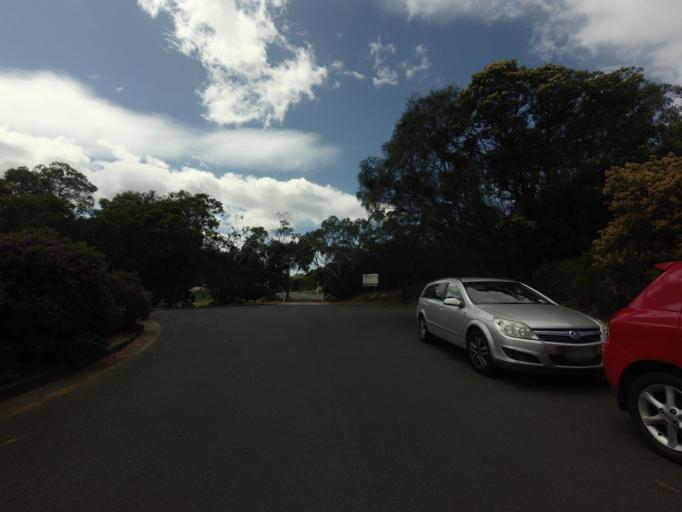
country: AU
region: Tasmania
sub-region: Clarence
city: Howrah
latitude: -42.8869
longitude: 147.4158
